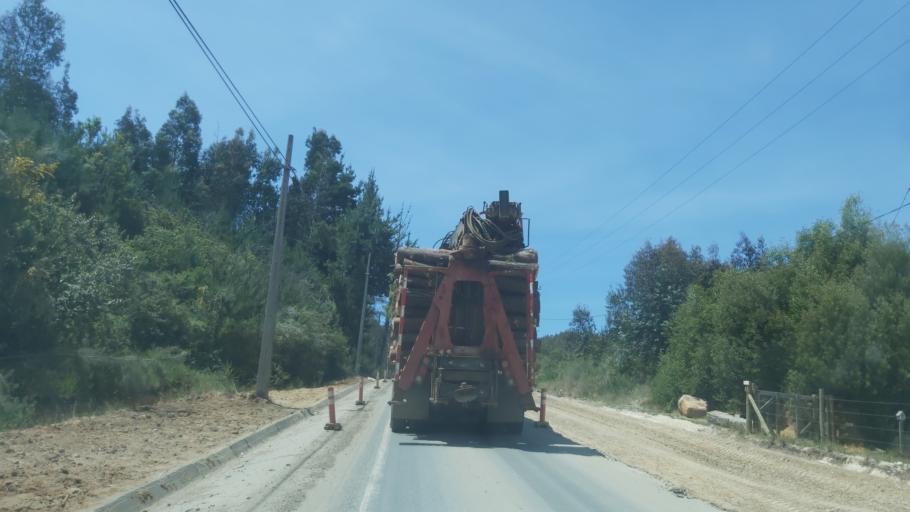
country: CL
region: Maule
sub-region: Provincia de Talca
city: Constitucion
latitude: -35.4464
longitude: -72.4679
